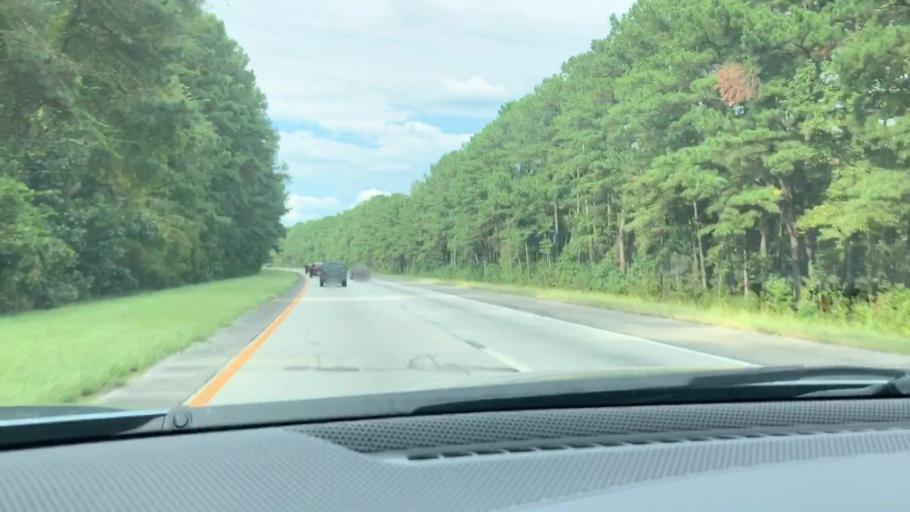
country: US
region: South Carolina
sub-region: Colleton County
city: Walterboro
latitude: 33.0204
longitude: -80.6654
